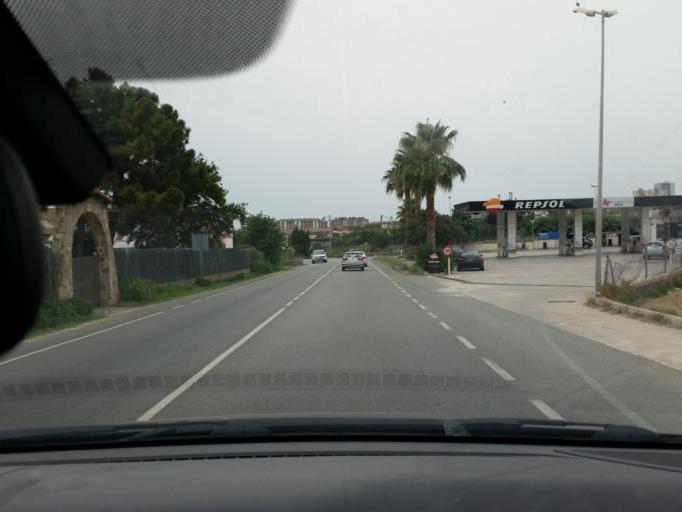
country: ES
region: Catalonia
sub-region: Provincia de Barcelona
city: Cabrera de Mar
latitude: 41.5151
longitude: 2.3953
